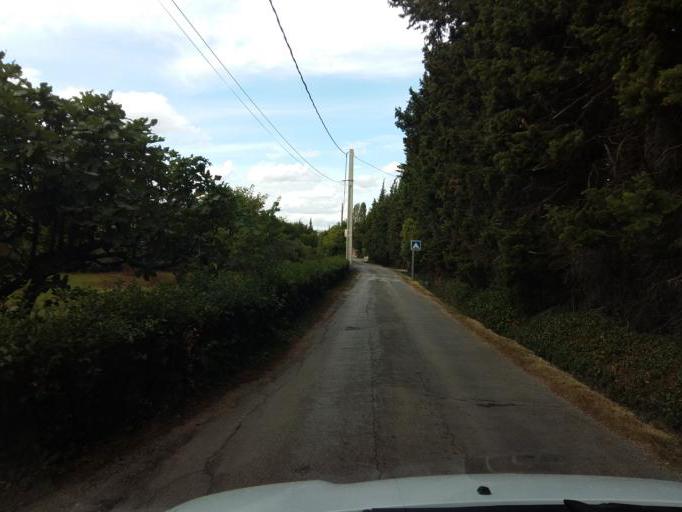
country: FR
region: Provence-Alpes-Cote d'Azur
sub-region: Departement du Vaucluse
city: Carpentras
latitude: 44.0379
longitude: 5.0345
